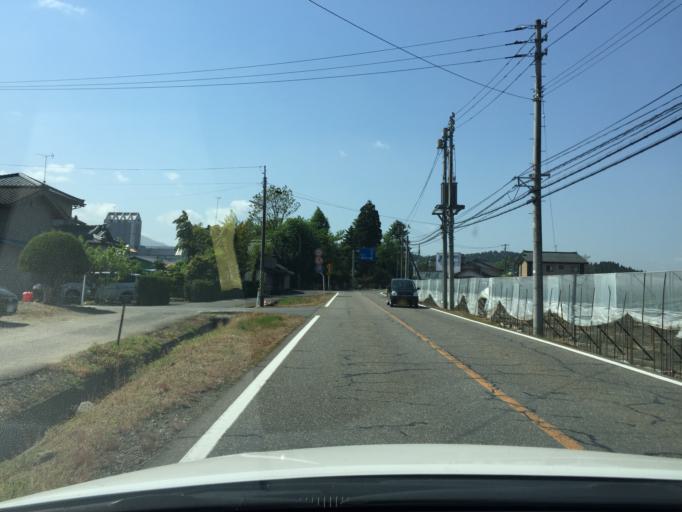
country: JP
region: Niigata
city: Muramatsu
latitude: 37.6743
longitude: 139.1495
